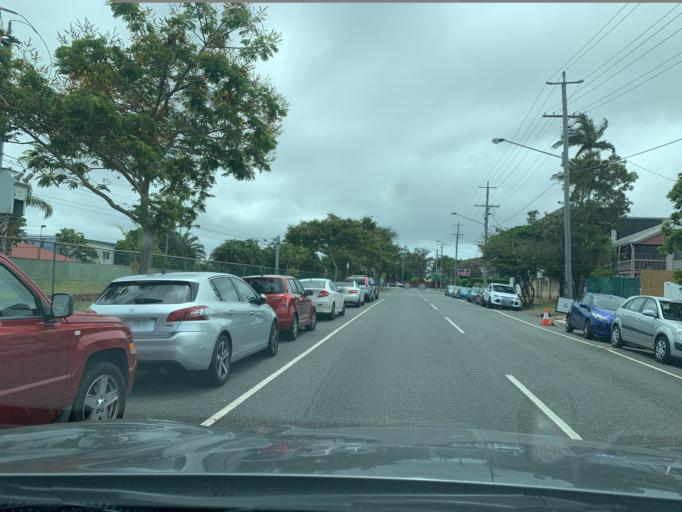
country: AU
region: Queensland
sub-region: Brisbane
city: Ascot
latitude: -27.4311
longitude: 153.0737
